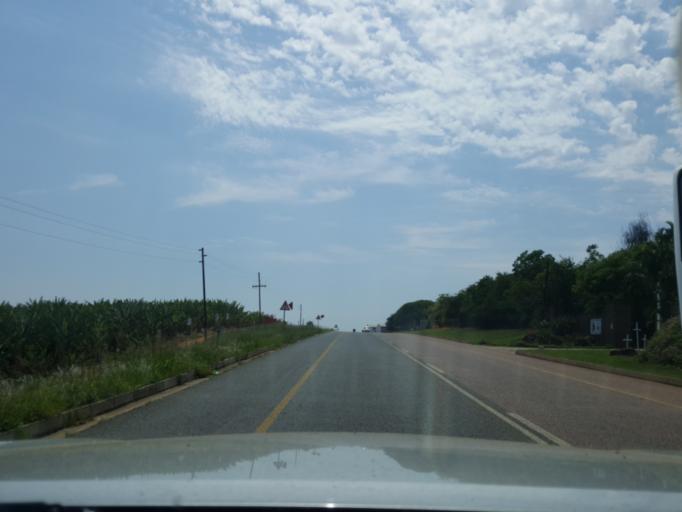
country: ZA
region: Mpumalanga
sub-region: Ehlanzeni District
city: White River
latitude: -25.0802
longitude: 31.0956
